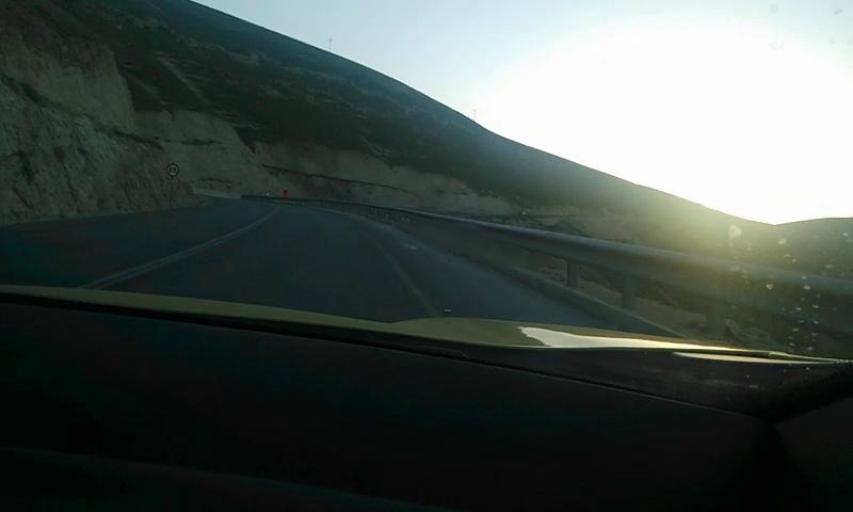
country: PS
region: West Bank
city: An Nuway`imah
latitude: 31.9103
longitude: 35.3699
